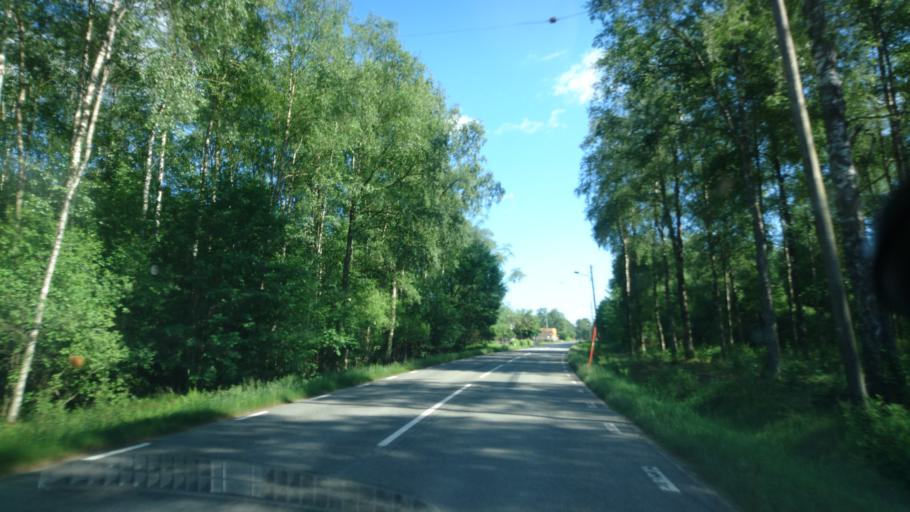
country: SE
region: Kronoberg
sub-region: Almhults Kommun
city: AElmhult
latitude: 56.4742
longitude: 14.2215
